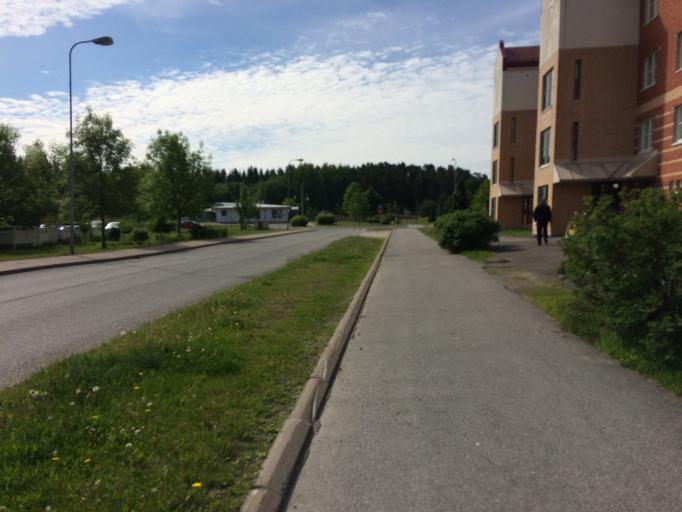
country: FI
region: Varsinais-Suomi
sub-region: Turku
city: Turku
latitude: 60.4726
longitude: 22.3157
